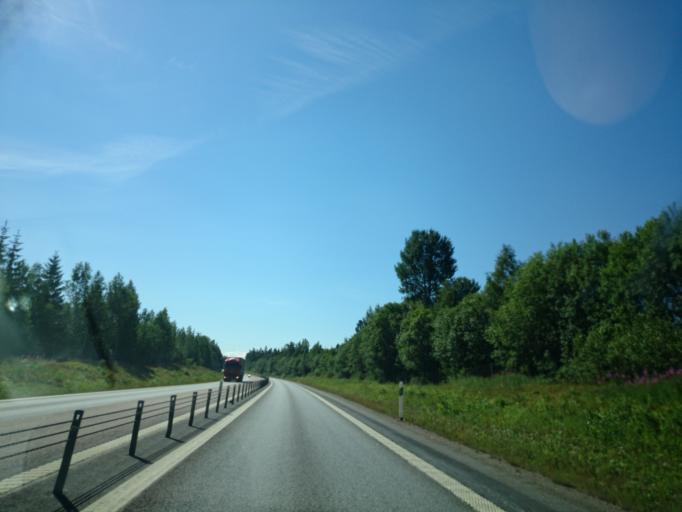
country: SE
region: Gaevleborg
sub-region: Gavle Kommun
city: Gavle
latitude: 60.7705
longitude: 17.0727
